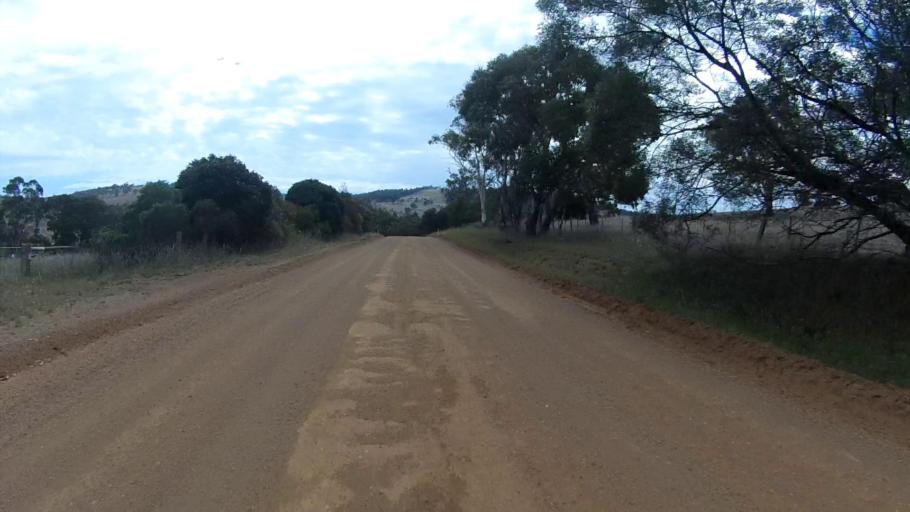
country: AU
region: Tasmania
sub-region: Sorell
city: Sorell
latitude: -42.6987
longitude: 147.4609
